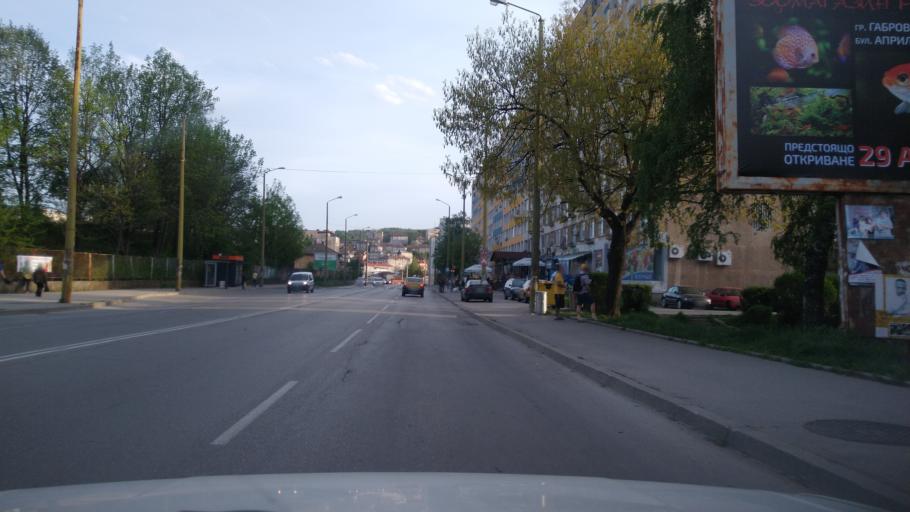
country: BG
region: Gabrovo
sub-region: Obshtina Gabrovo
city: Gabrovo
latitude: 42.8838
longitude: 25.3129
